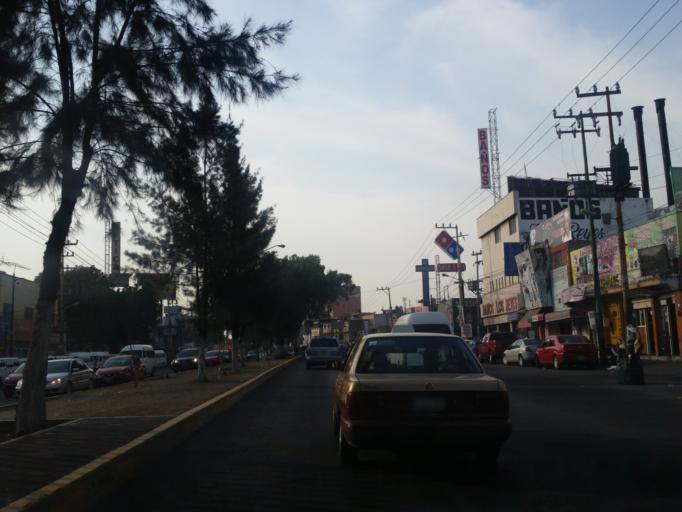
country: MX
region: Mexico
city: Los Reyes La Paz
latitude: 19.3548
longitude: -98.9781
